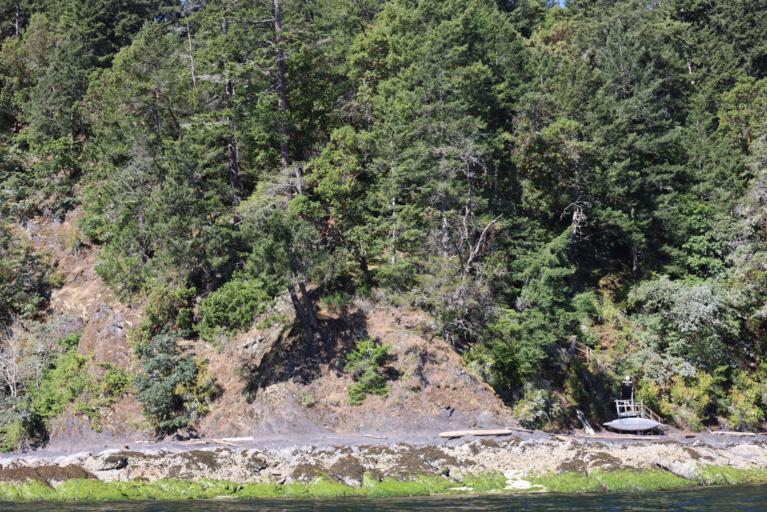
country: CA
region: British Columbia
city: North Cowichan
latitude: 48.8097
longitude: -123.6053
